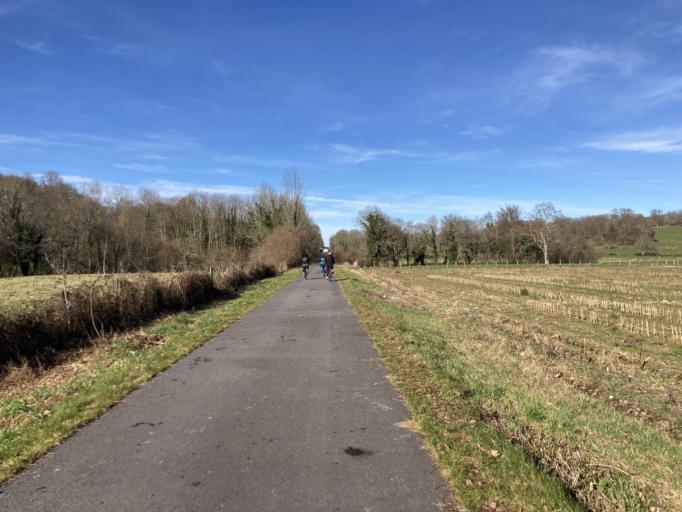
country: FR
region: Aquitaine
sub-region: Departement des Pyrenees-Atlantiques
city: Arudy
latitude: 43.1209
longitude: -0.4386
